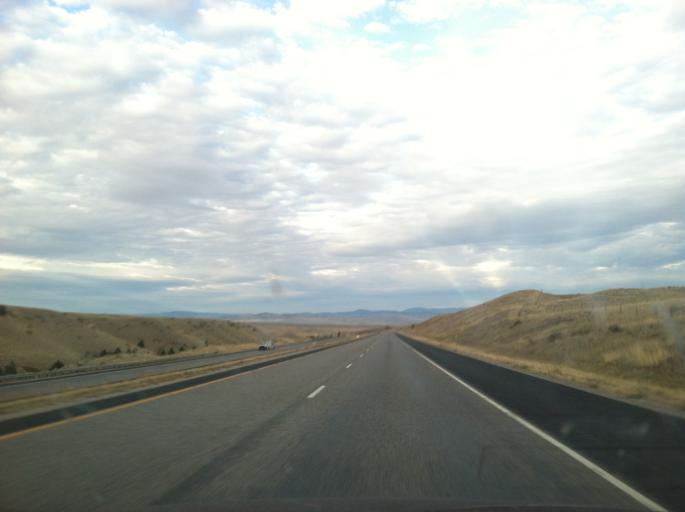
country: US
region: Montana
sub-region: Jefferson County
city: Whitehall
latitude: 45.8961
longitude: -111.8352
